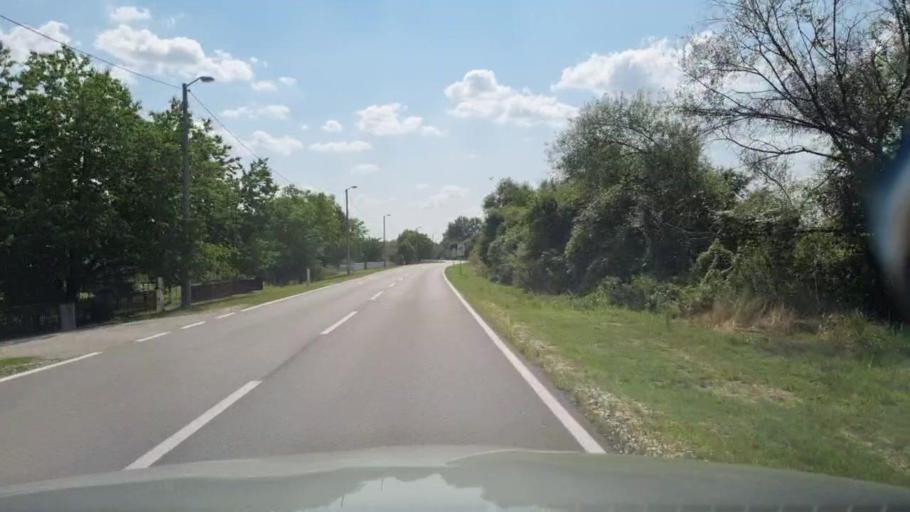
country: HR
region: Brodsko-Posavska
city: Krusevica
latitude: 45.0410
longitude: 18.5320
